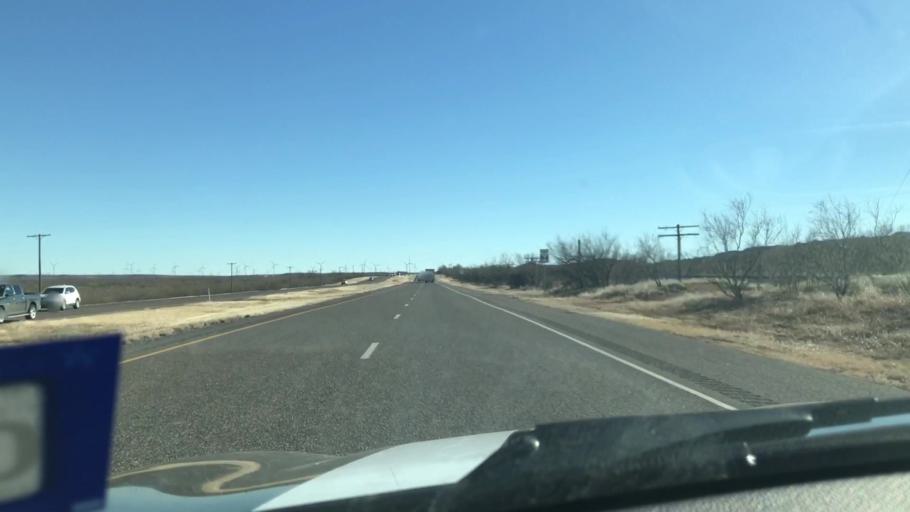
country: US
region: Texas
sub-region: Scurry County
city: Snyder
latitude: 32.9607
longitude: -101.0915
